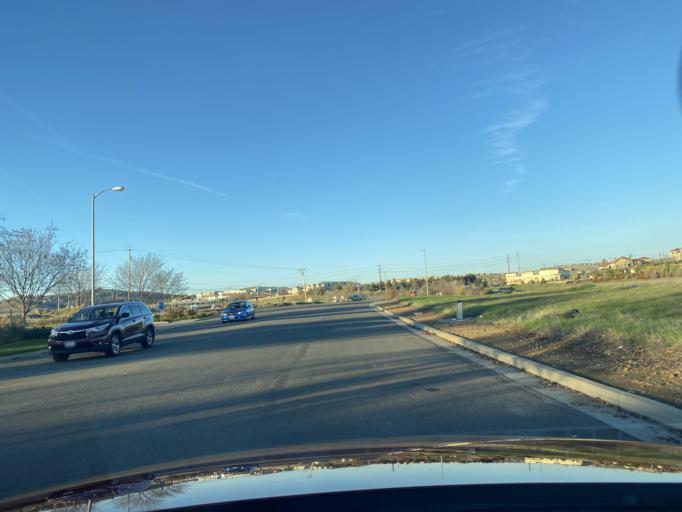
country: US
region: California
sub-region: El Dorado County
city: El Dorado Hills
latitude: 38.6419
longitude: -121.0706
